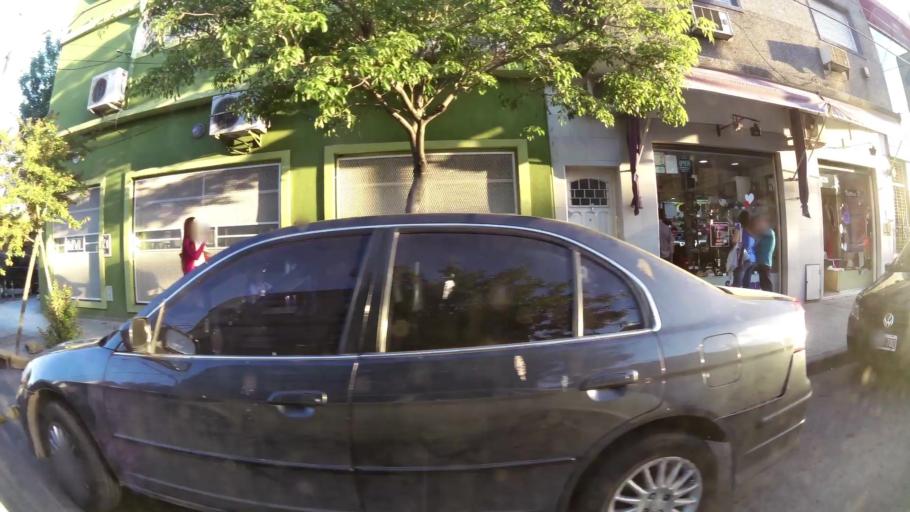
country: AR
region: Buenos Aires
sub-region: Partido de General San Martin
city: General San Martin
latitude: -34.5487
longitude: -58.5058
